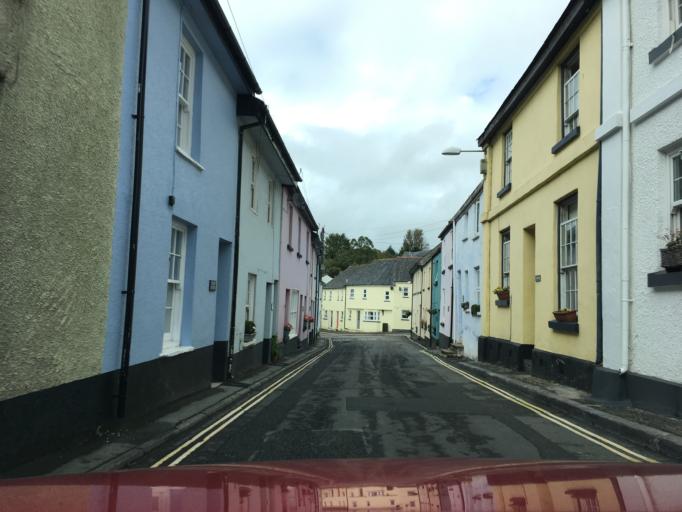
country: GB
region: England
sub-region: Devon
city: Modbury
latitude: 50.3137
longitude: -3.8361
